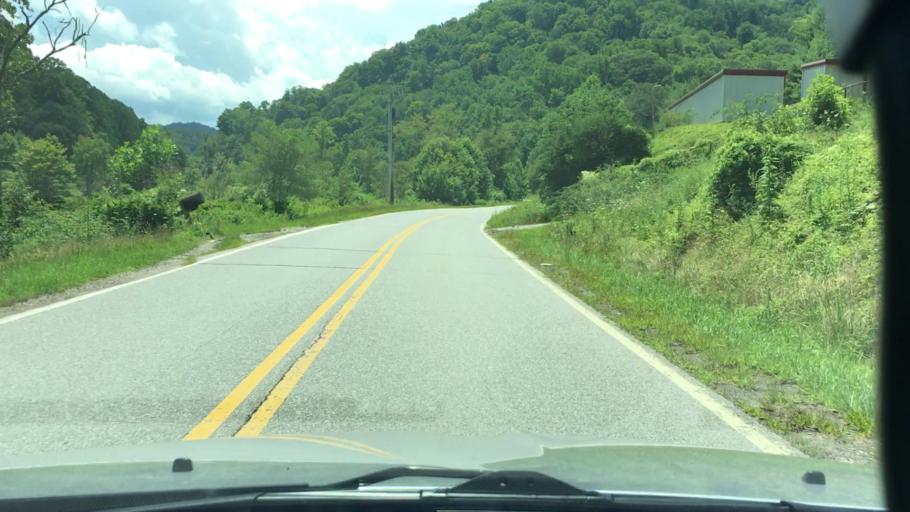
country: US
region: North Carolina
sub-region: Madison County
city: Mars Hill
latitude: 35.9332
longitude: -82.5328
